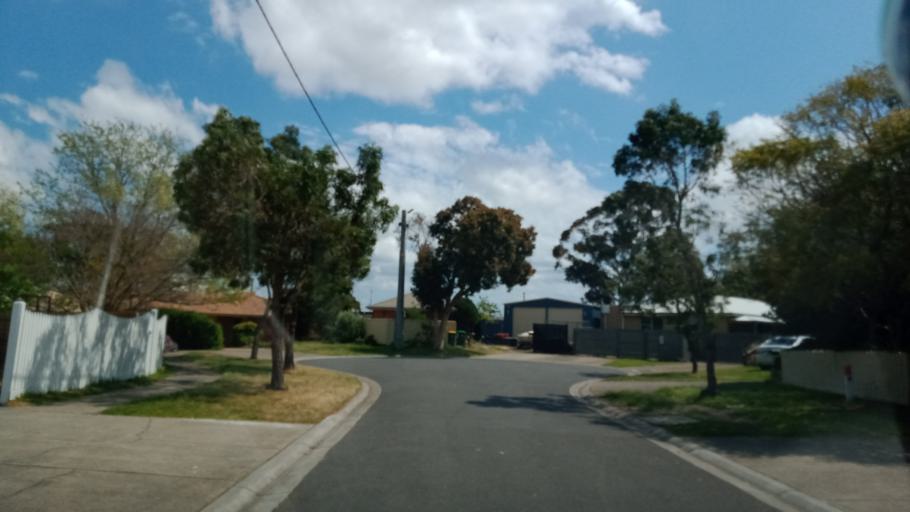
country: AU
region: Victoria
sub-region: Frankston
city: Sandhurst
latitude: -38.0956
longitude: 145.1996
